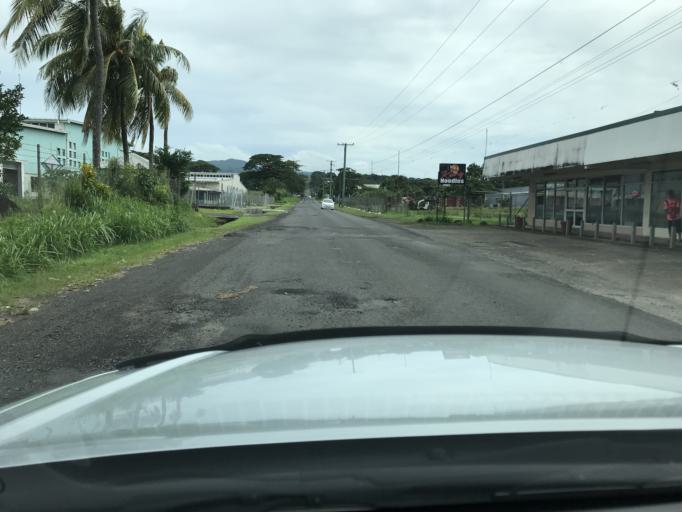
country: WS
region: Tuamasaga
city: Vaiusu
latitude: -13.8222
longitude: -171.8054
